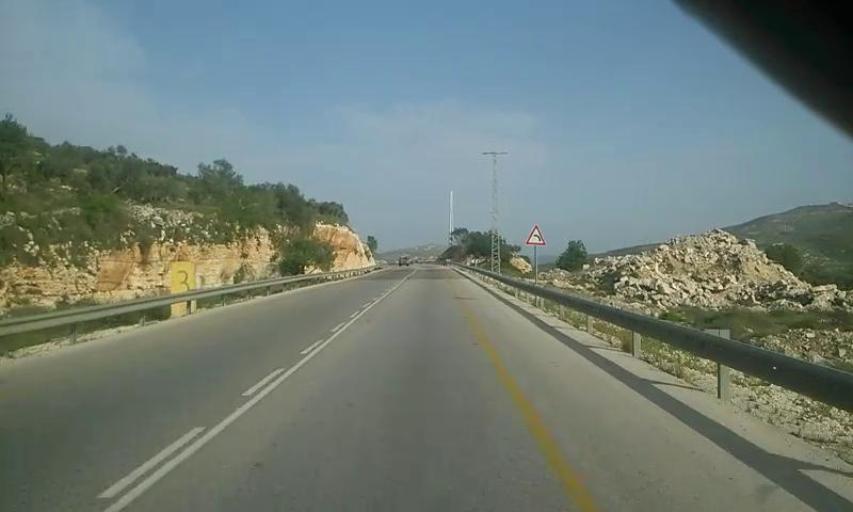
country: PS
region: West Bank
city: `Asirah al Qibliyah
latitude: 32.1877
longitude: 35.2185
